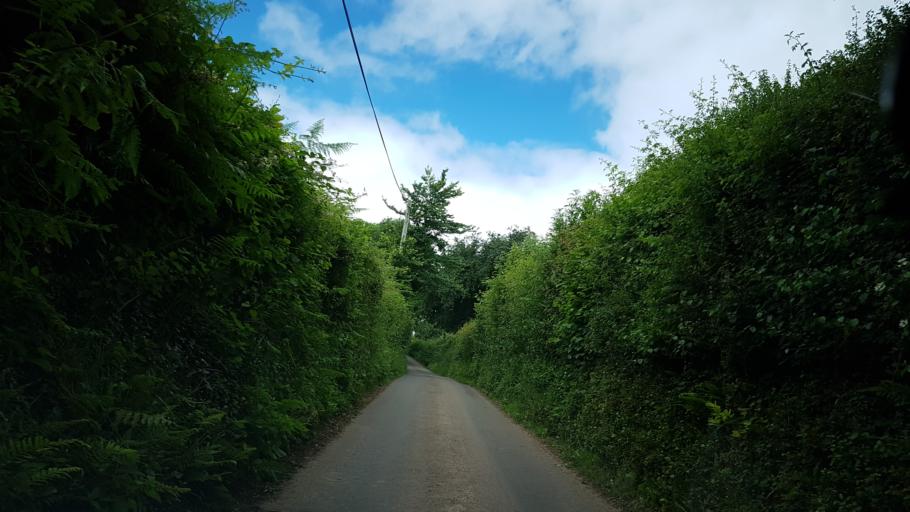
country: GB
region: Wales
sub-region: Monmouthshire
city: Llanarth
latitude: 51.8442
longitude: -2.8989
